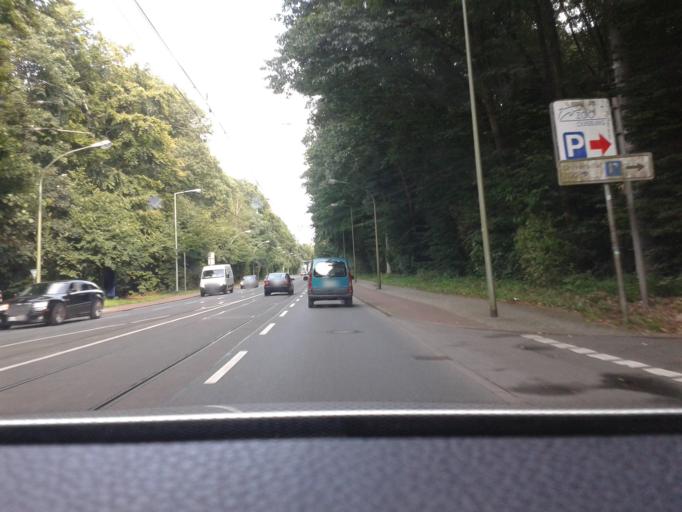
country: DE
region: North Rhine-Westphalia
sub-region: Regierungsbezirk Dusseldorf
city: Duisburg
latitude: 51.4330
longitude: 6.8116
